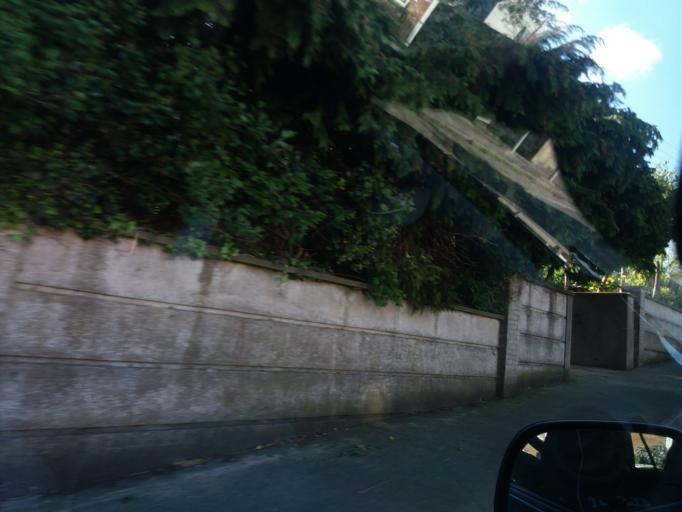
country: IE
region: Munster
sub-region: Waterford
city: Waterford
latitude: 52.2660
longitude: -7.1064
